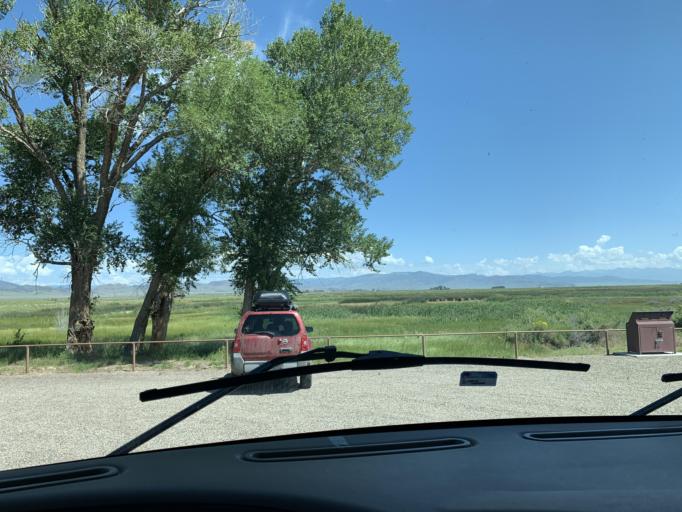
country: US
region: Colorado
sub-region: Saguache County
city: Saguache
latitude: 37.9382
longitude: -106.1439
